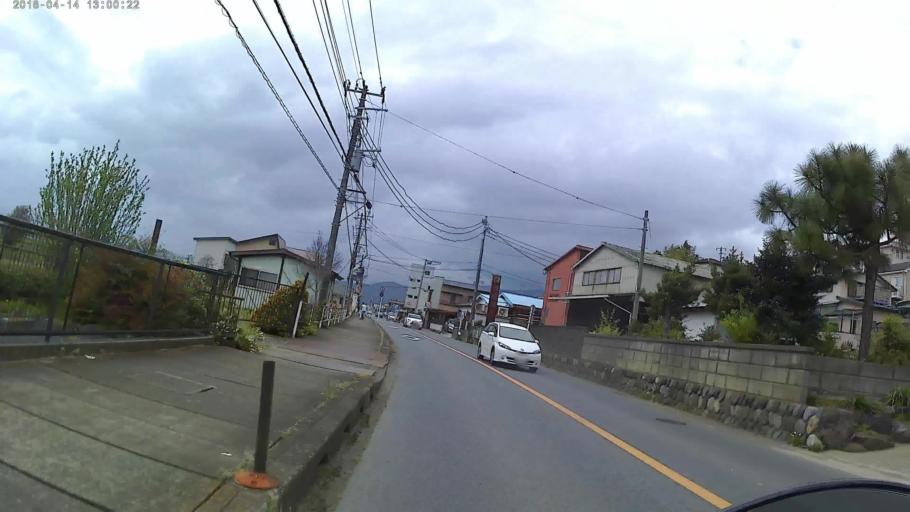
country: JP
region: Kanagawa
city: Isehara
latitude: 35.3721
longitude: 139.3059
